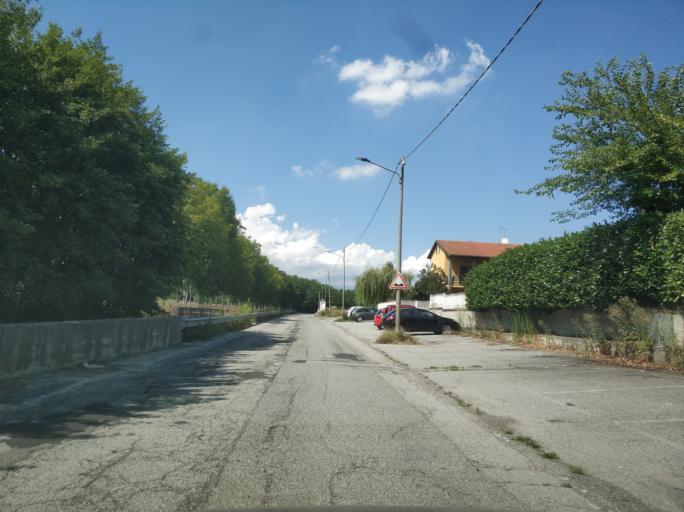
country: IT
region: Piedmont
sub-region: Provincia di Torino
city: Feletto
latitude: 45.2961
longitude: 7.7214
